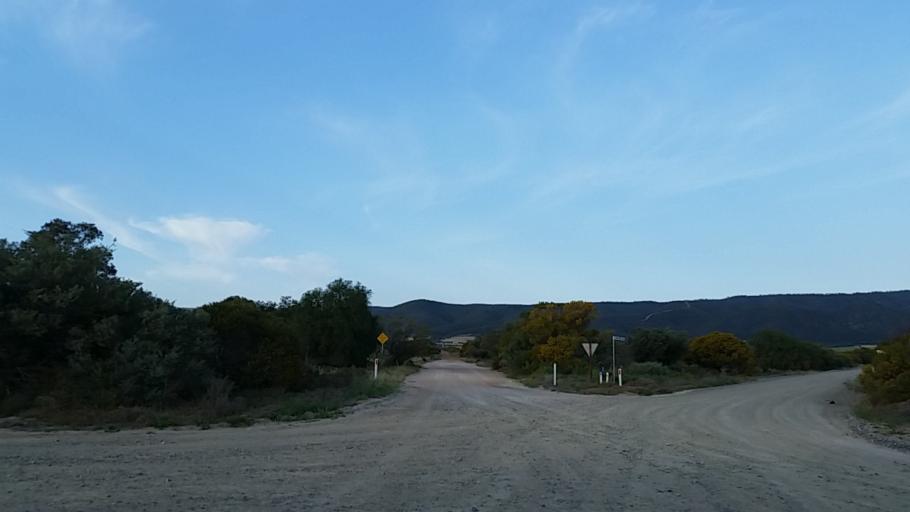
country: AU
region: South Australia
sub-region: Port Pirie City and Dists
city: Port Pirie
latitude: -33.0546
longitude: 138.0681
